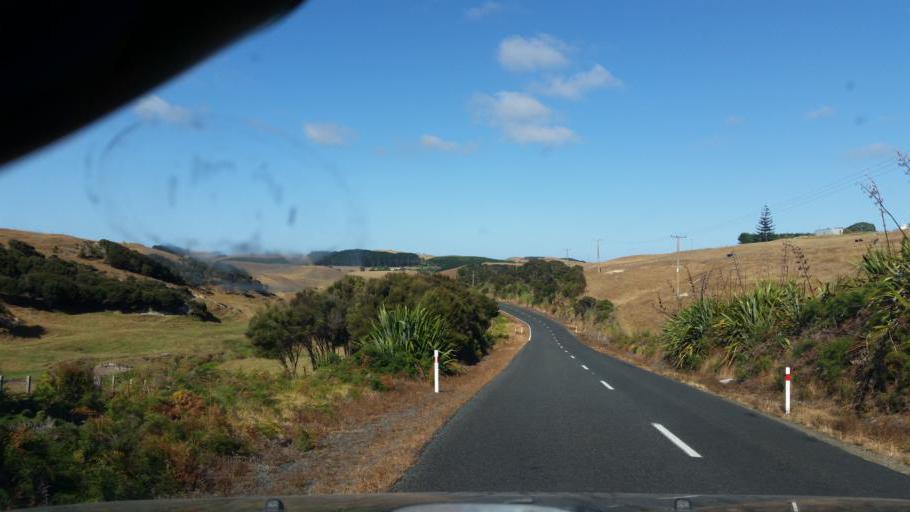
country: NZ
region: Northland
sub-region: Kaipara District
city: Dargaville
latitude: -35.8272
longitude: 173.6727
